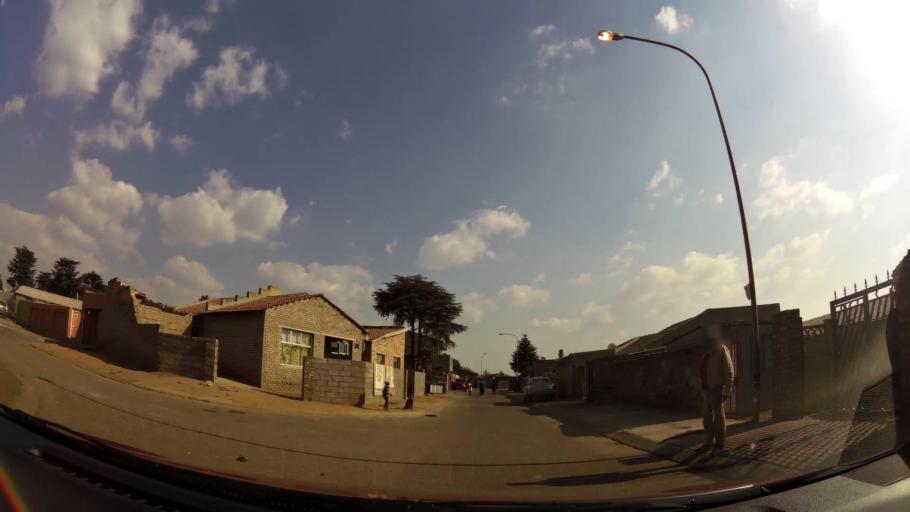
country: ZA
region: Gauteng
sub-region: City of Johannesburg Metropolitan Municipality
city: Soweto
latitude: -26.2396
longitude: 27.9466
